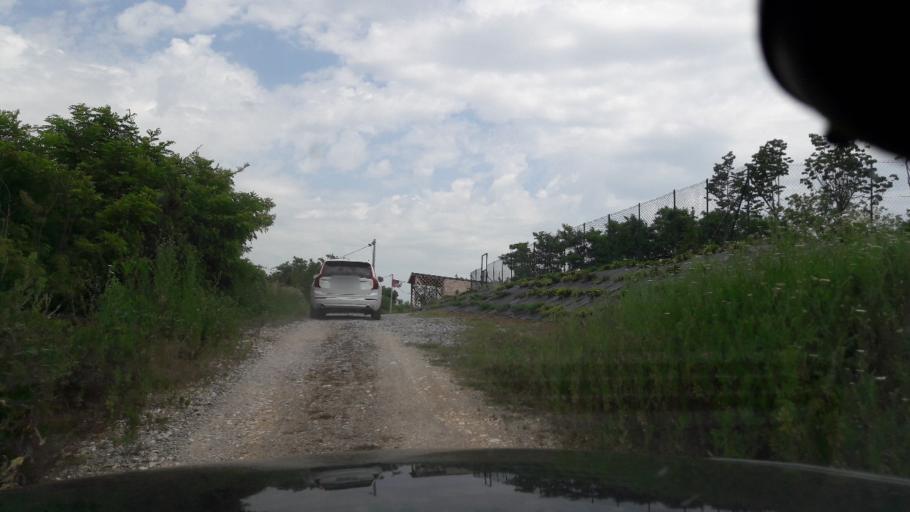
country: RS
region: Central Serbia
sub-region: Belgrade
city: Sopot
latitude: 44.6020
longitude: 20.5992
